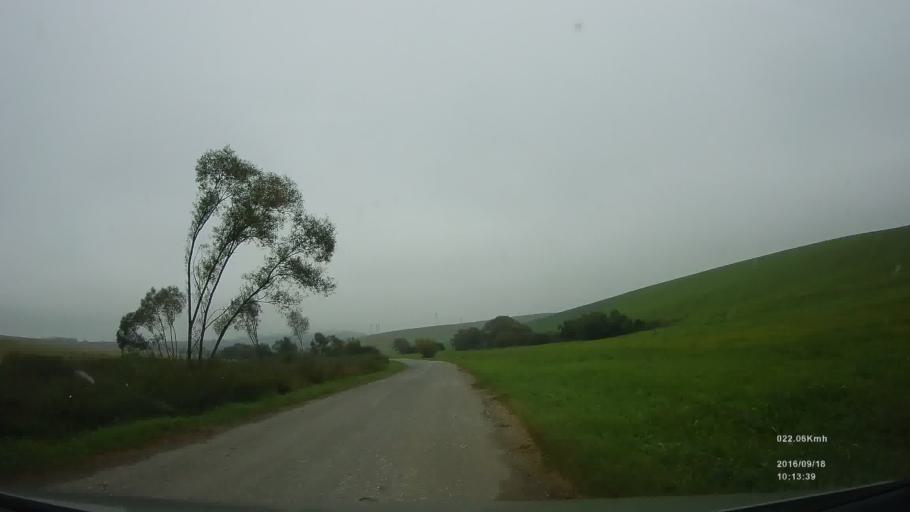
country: SK
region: Kosicky
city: Spisska Nova Ves
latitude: 48.9359
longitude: 20.6315
